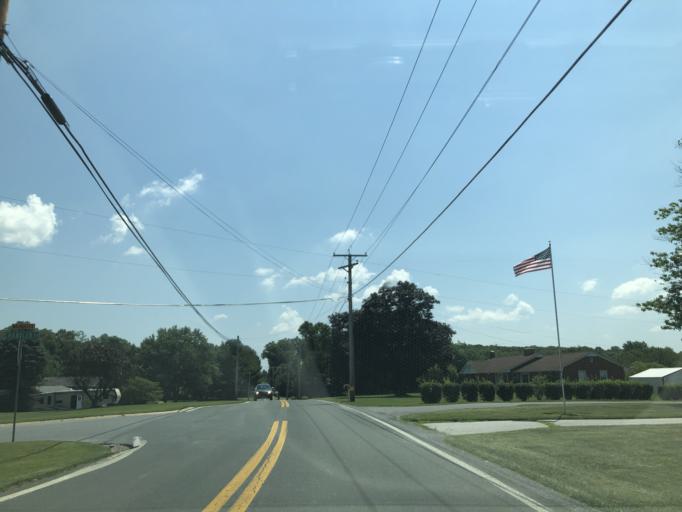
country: US
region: Maryland
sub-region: Carroll County
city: Westminster
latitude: 39.5386
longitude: -76.9770
